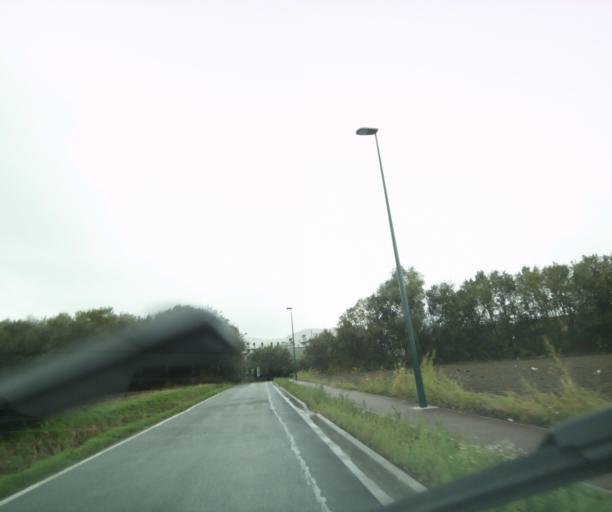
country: FR
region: Nord-Pas-de-Calais
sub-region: Departement du Nord
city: Roncq
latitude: 50.7456
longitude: 3.1255
